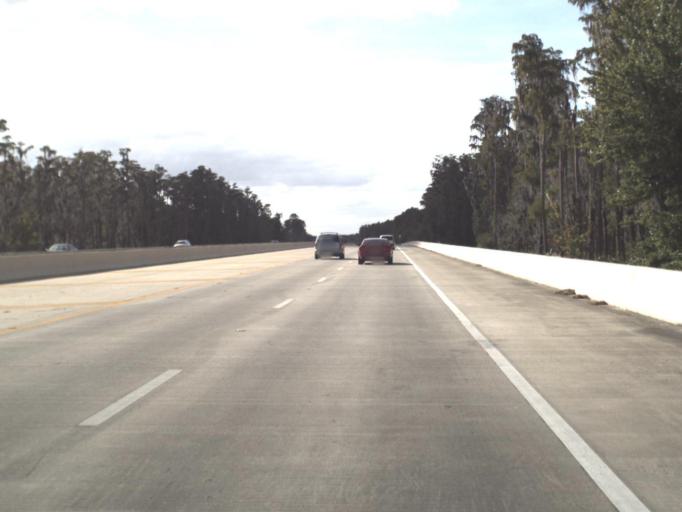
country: US
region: Florida
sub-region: Orange County
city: Hunters Creek
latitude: 28.3468
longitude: -81.4462
